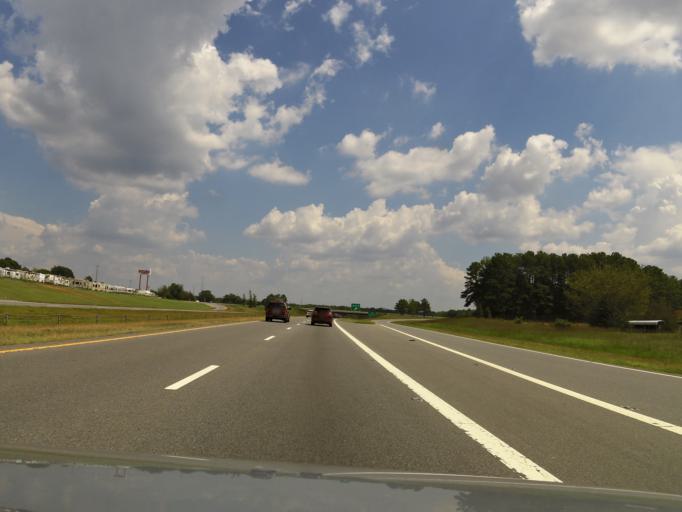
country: US
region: North Carolina
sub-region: Cleveland County
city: Kings Mountain
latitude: 35.2591
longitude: -81.3648
